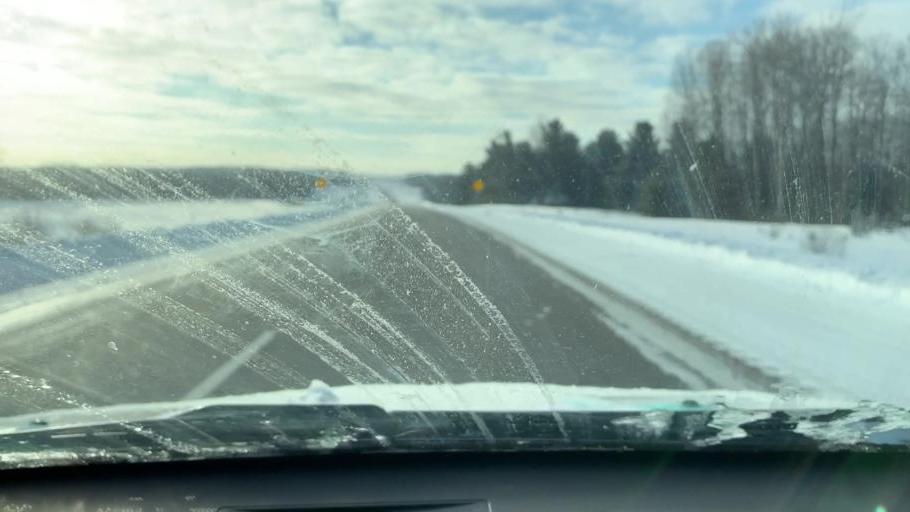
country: US
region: Michigan
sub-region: Wexford County
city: Manton
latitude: 44.3316
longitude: -85.4059
